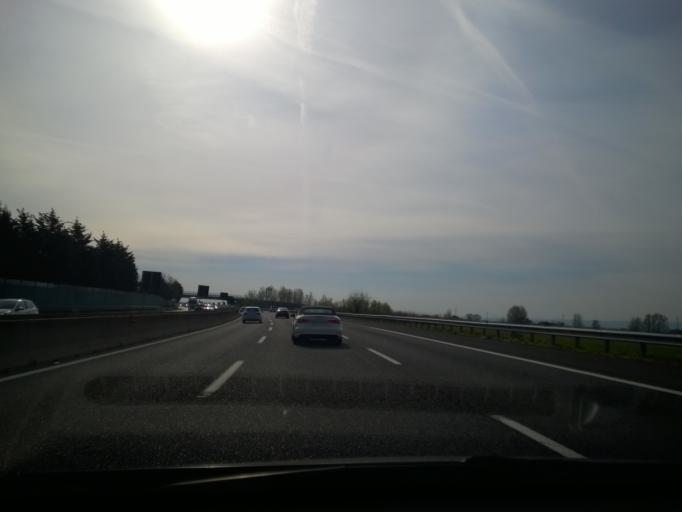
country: IT
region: Emilia-Romagna
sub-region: Forli-Cesena
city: Forlimpopoli
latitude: 44.2294
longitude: 12.1468
